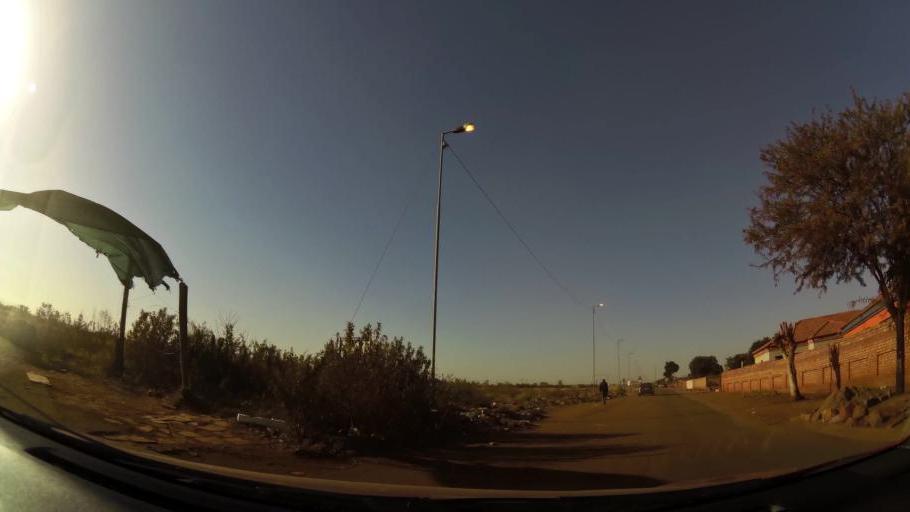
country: ZA
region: Gauteng
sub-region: City of Tshwane Metropolitan Municipality
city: Mabopane
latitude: -25.5868
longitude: 28.0945
